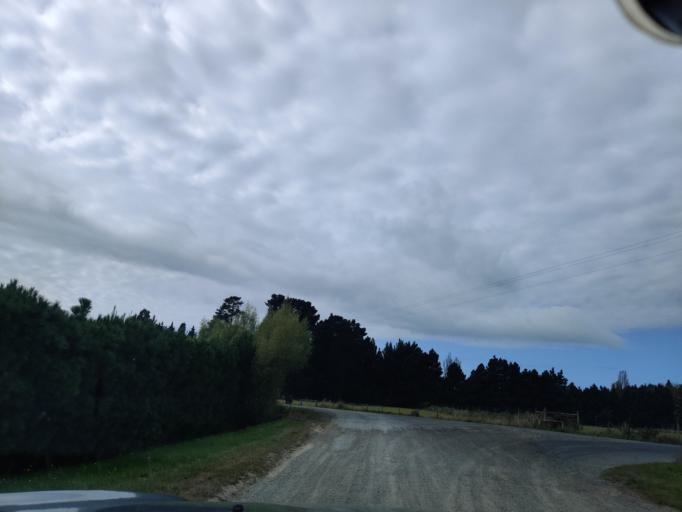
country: NZ
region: Canterbury
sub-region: Hurunui District
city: Amberley
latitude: -43.2296
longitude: 172.7172
